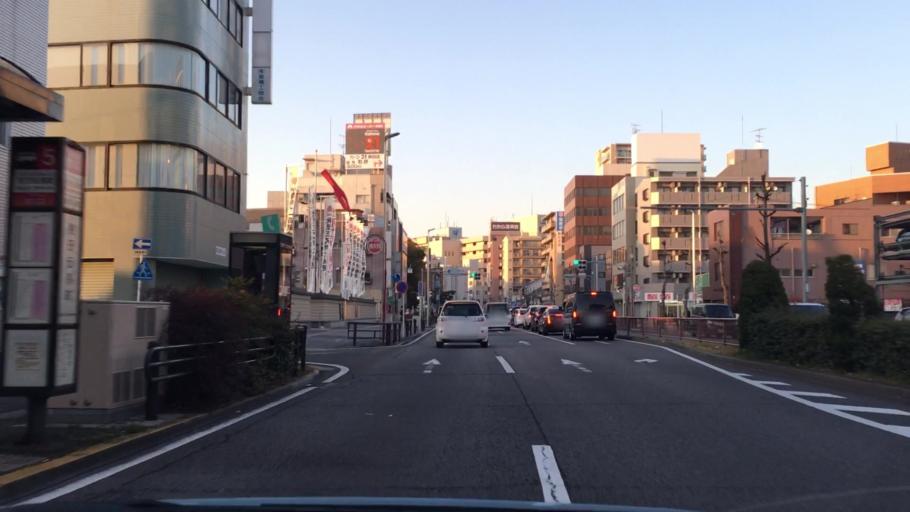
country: JP
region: Aichi
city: Nagoya-shi
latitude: 35.1221
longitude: 136.9111
